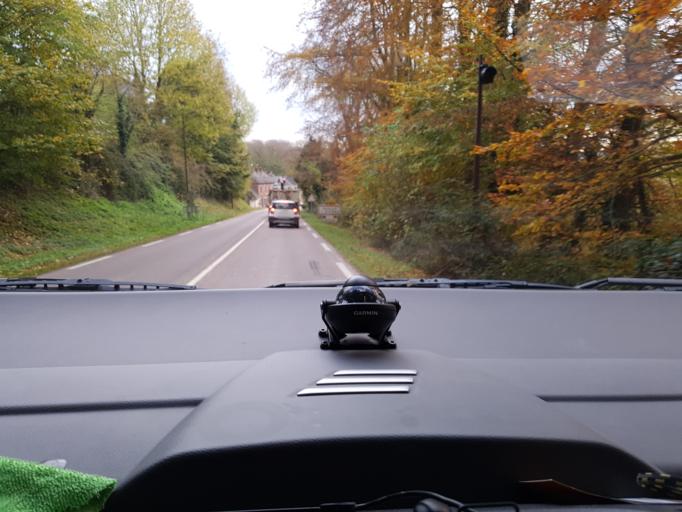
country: FR
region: Haute-Normandie
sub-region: Departement de la Seine-Maritime
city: Varengeville-sur-Mer
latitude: 49.8754
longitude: 0.9605
